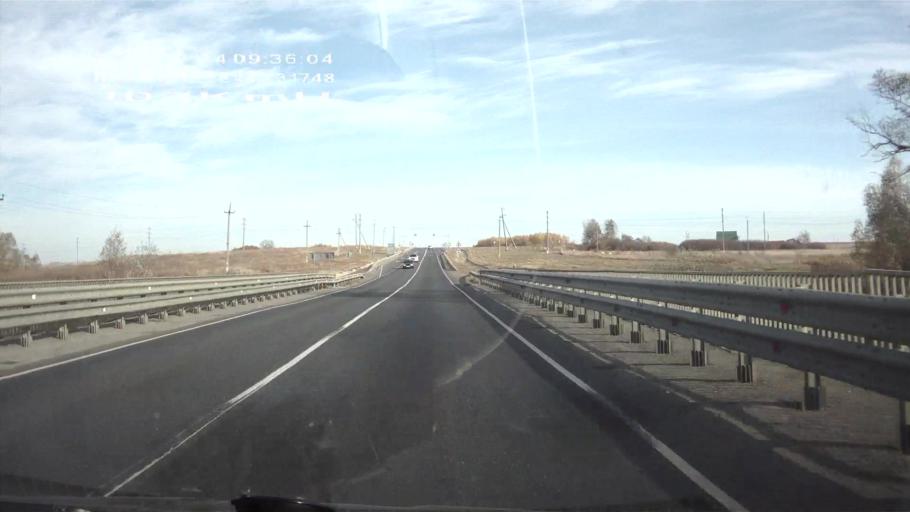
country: RU
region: Penza
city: Mokshan
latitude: 53.6134
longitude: 44.7318
